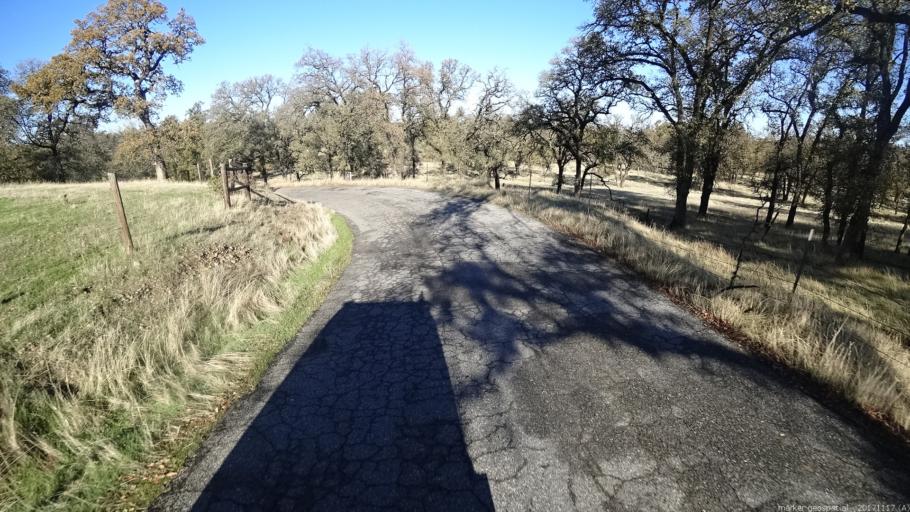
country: US
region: California
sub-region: Shasta County
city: Cottonwood
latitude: 40.4370
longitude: -122.1888
